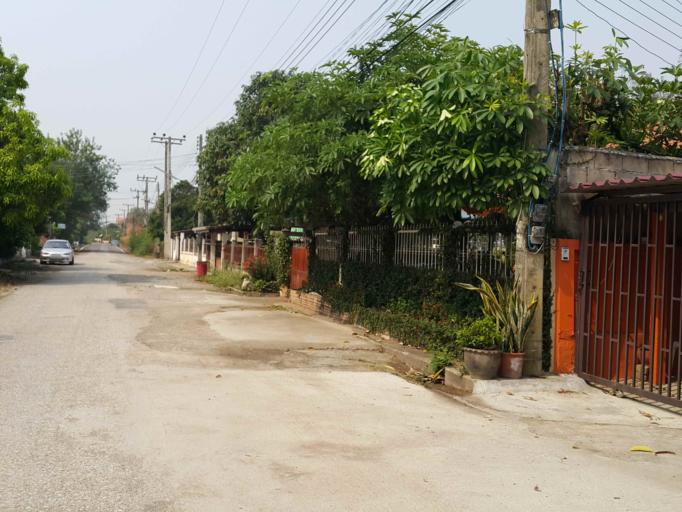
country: TH
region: Chiang Mai
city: Saraphi
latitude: 18.7631
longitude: 99.0638
